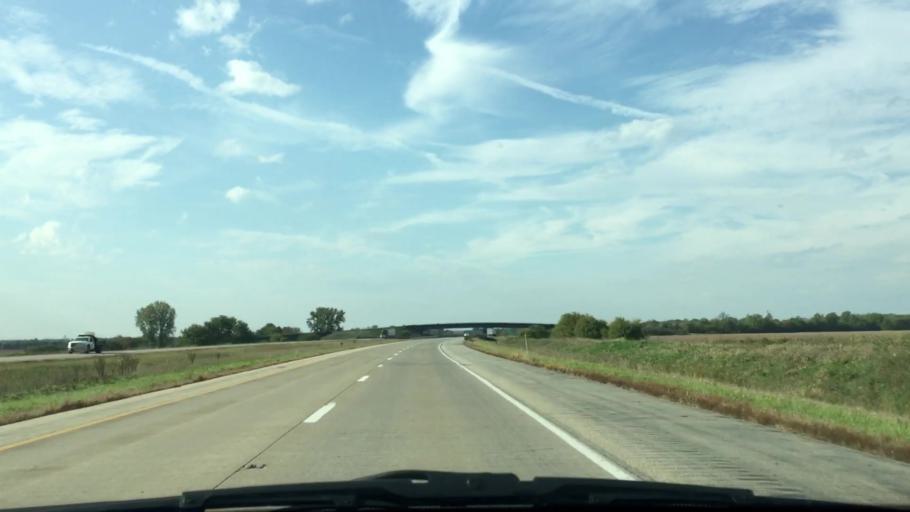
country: US
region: Illinois
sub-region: Whiteside County
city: Erie
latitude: 41.6465
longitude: -90.1598
